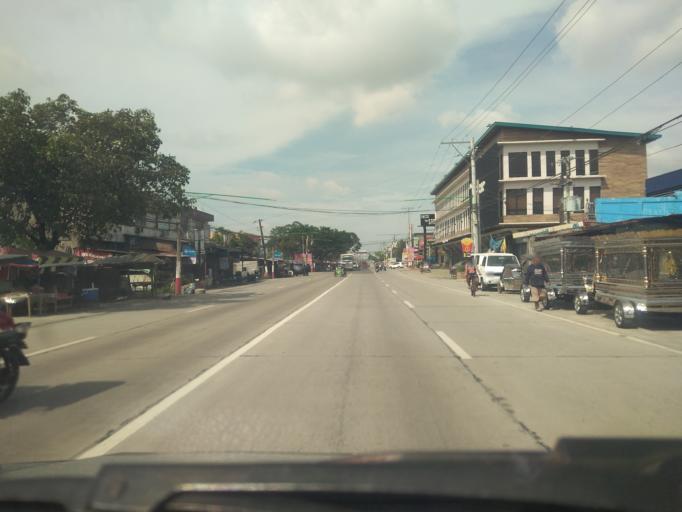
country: PH
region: Central Luzon
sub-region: Province of Pampanga
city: San Fernando
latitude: 15.0126
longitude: 120.7067
